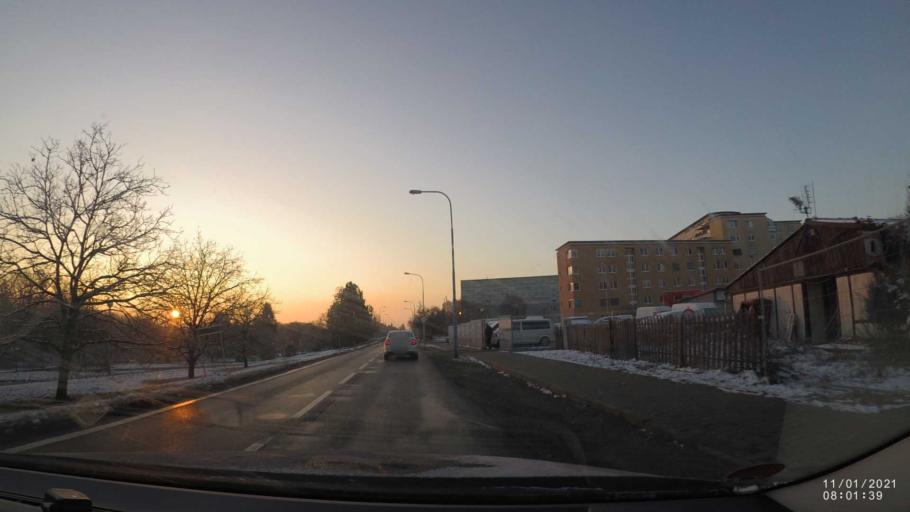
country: CZ
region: South Moravian
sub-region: Mesto Brno
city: Mokra Hora
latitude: 49.2358
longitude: 16.6280
